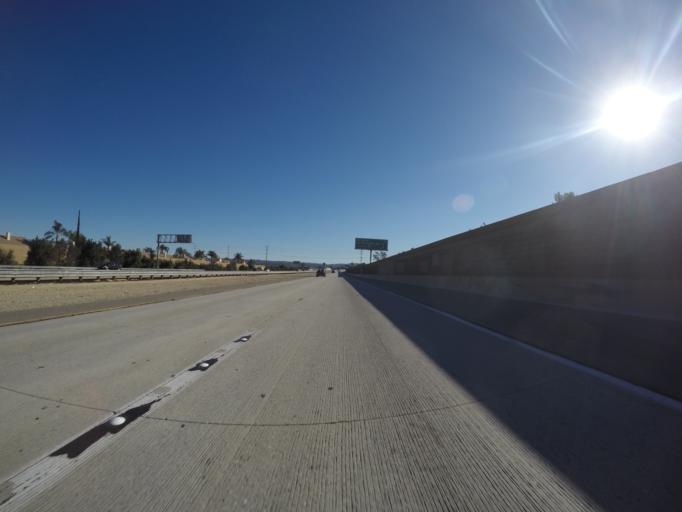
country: US
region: California
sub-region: San Bernardino County
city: Highland
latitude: 34.1166
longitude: -117.2008
